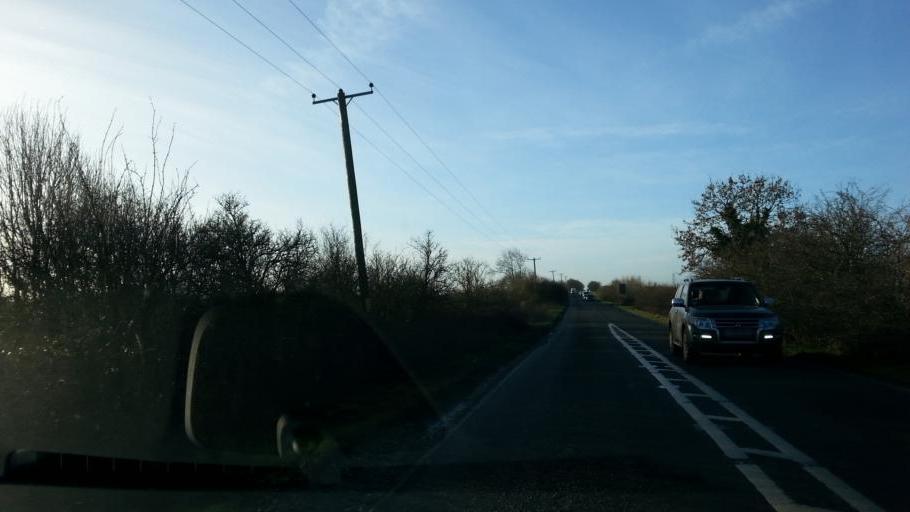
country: GB
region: England
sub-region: Lincolnshire
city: Grantham
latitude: 52.9334
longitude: -0.5677
